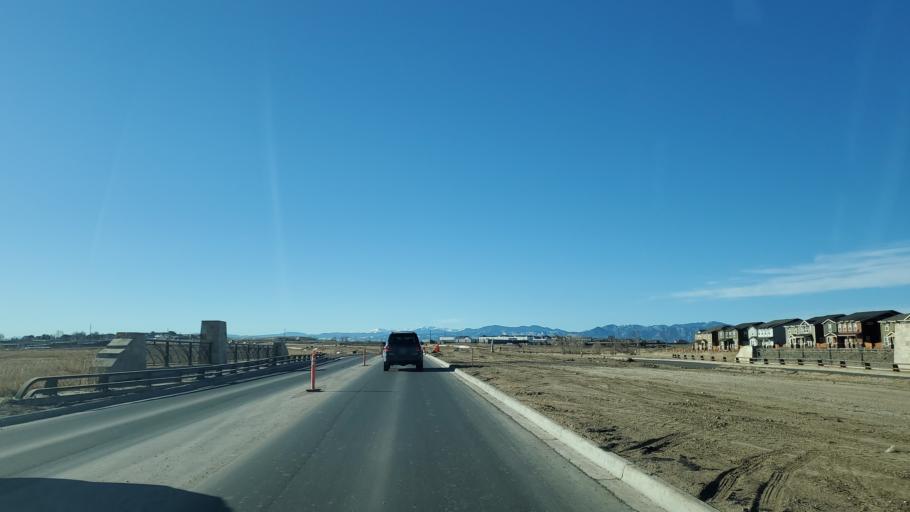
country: US
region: Colorado
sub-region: Boulder County
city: Erie
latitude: 39.9935
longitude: -105.0116
